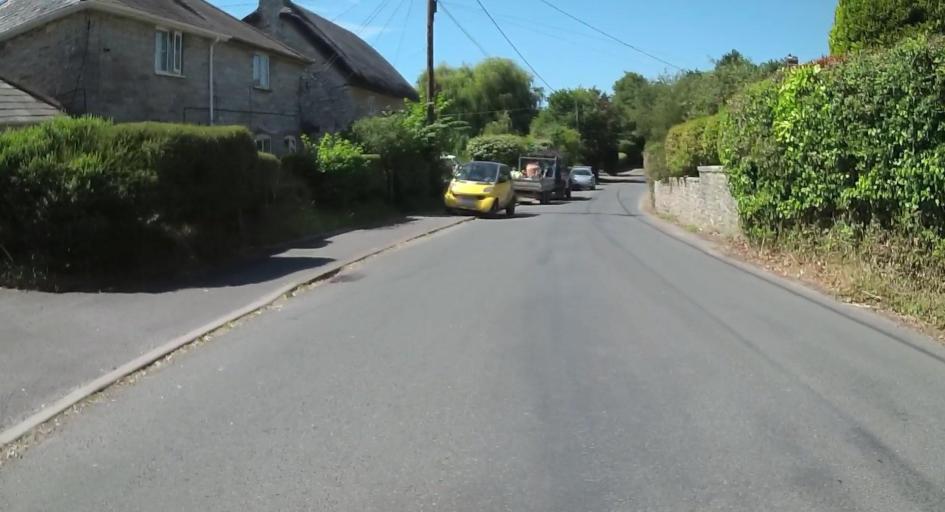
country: GB
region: England
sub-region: Dorset
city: Wareham
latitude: 50.6359
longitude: -2.0865
